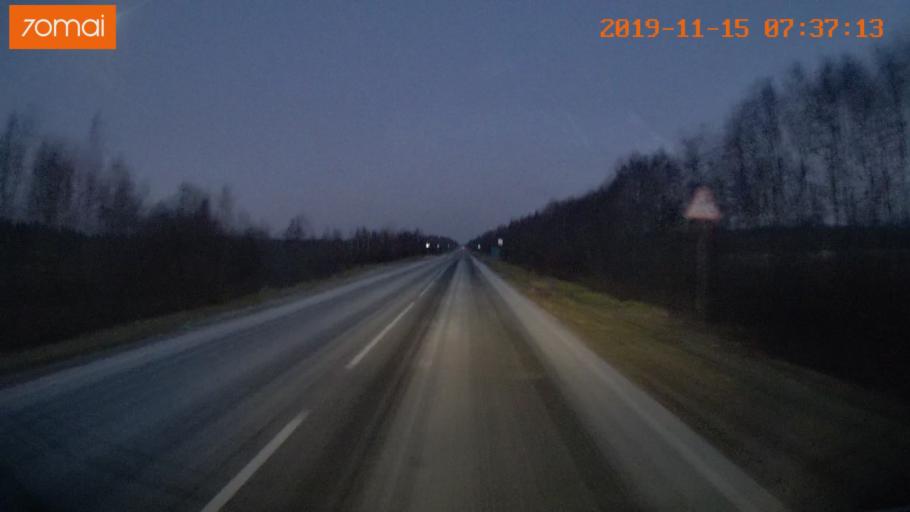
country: RU
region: Vologda
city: Sheksna
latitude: 58.7461
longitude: 38.4228
